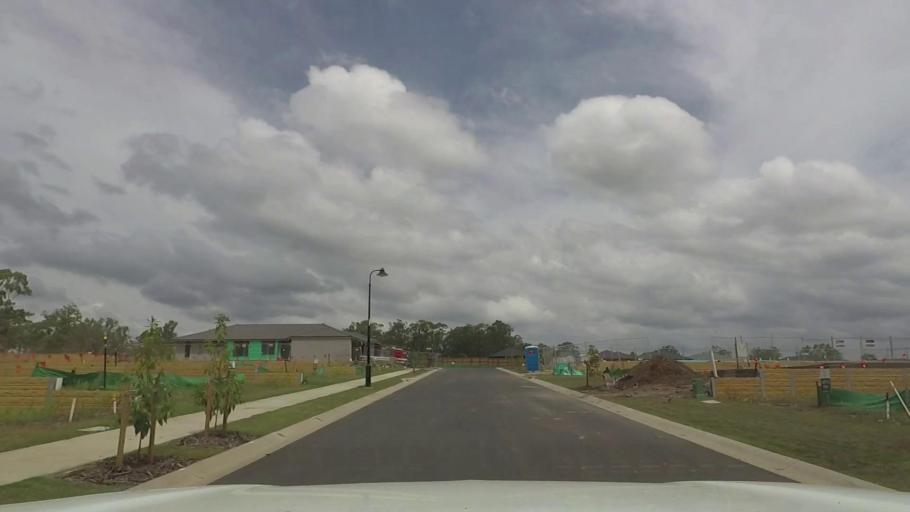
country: AU
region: Queensland
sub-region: Logan
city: Waterford West
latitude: -27.7019
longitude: 153.1077
